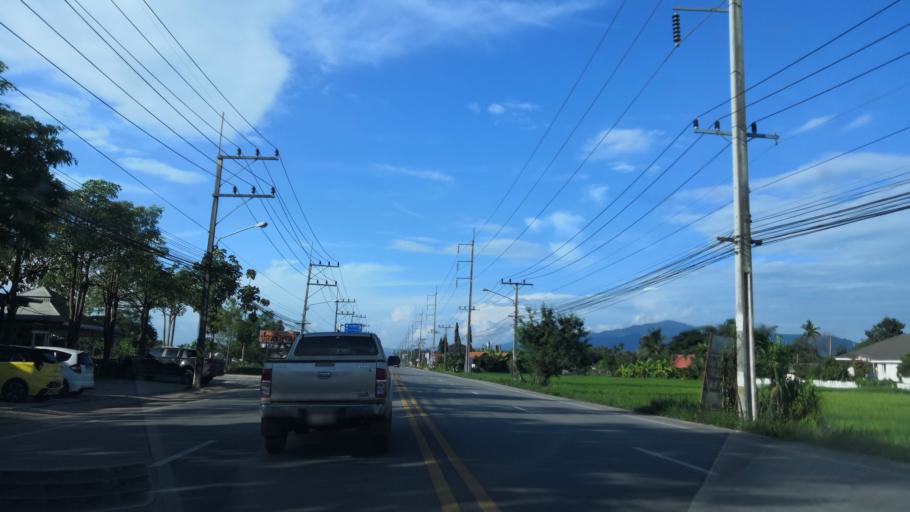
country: TH
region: Chiang Rai
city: Wiang Pa Pao
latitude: 19.3168
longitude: 99.5122
